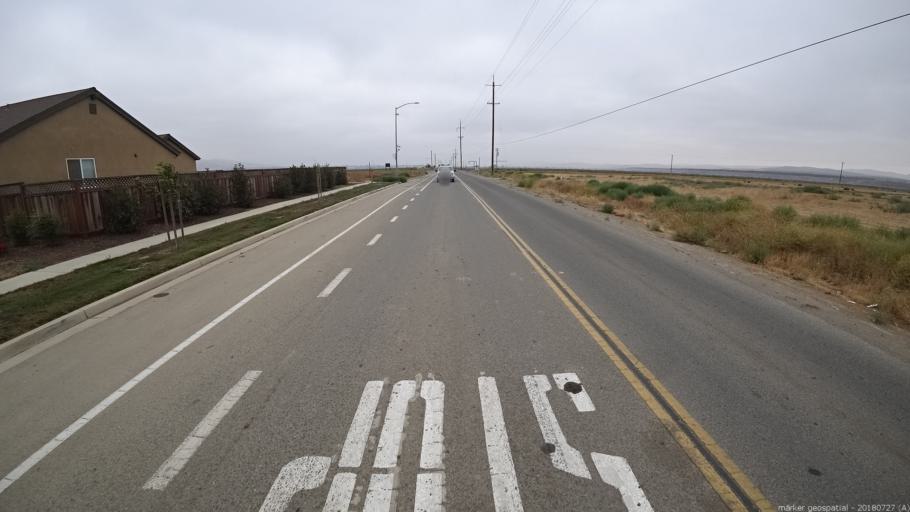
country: US
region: California
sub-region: Monterey County
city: King City
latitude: 36.2235
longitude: -121.1353
